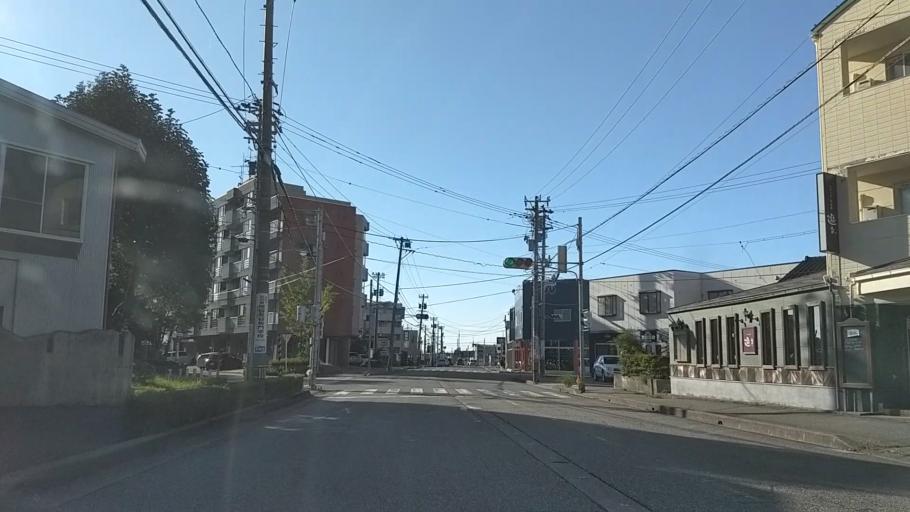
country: JP
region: Ishikawa
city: Kanazawa-shi
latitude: 36.5712
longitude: 136.6412
